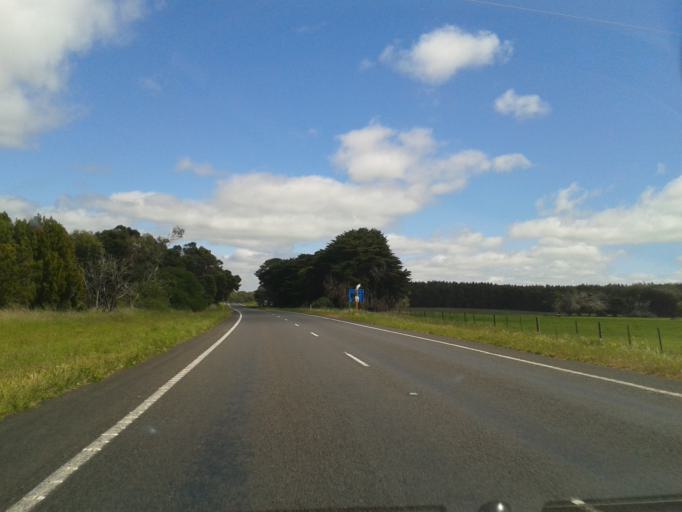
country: AU
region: Victoria
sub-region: Glenelg
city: Portland
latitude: -38.2429
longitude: 141.8727
